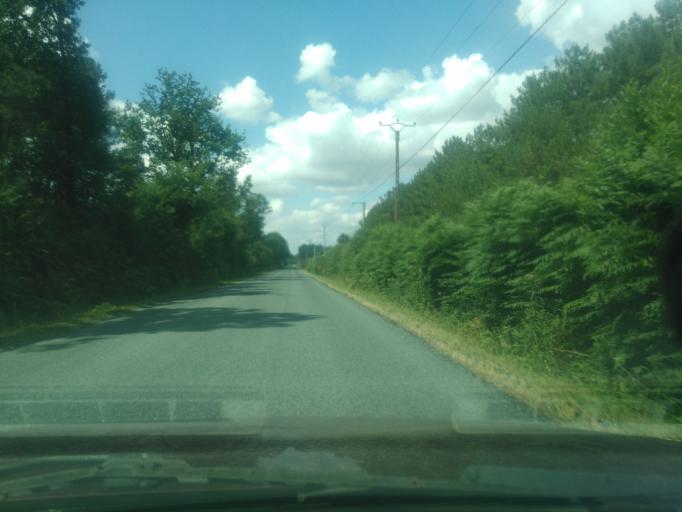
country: FR
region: Pays de la Loire
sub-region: Departement de la Vendee
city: Les Brouzils
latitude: 46.8697
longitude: -1.3171
